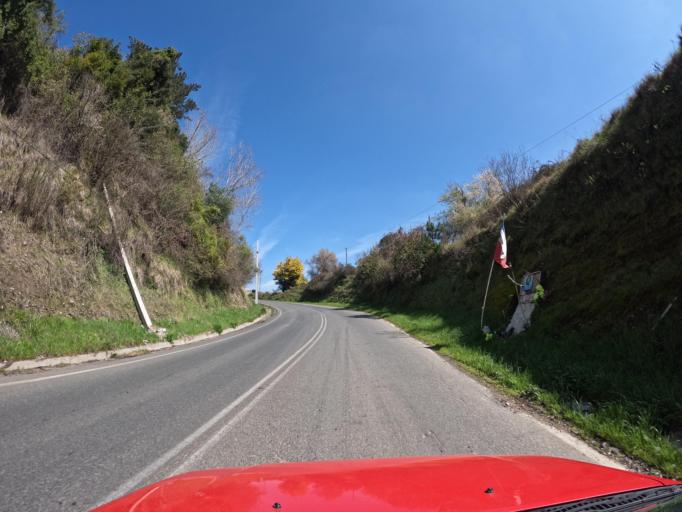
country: CL
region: Maule
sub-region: Provincia de Talca
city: San Clemente
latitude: -35.4693
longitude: -71.2759
